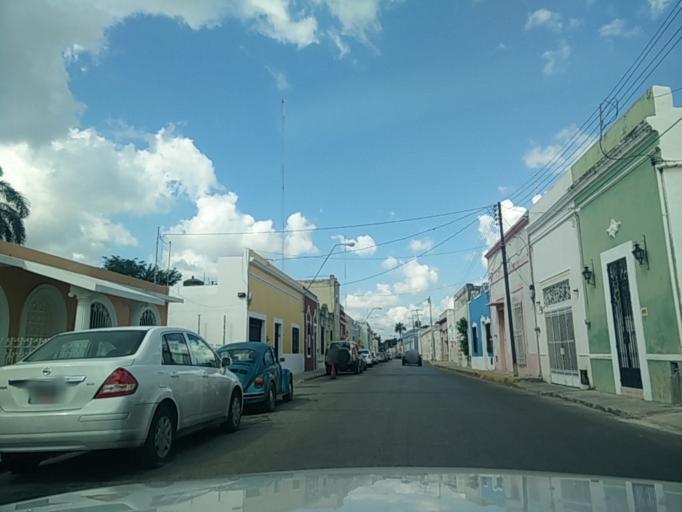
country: MX
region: Yucatan
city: Merida
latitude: 20.9817
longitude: -89.6191
